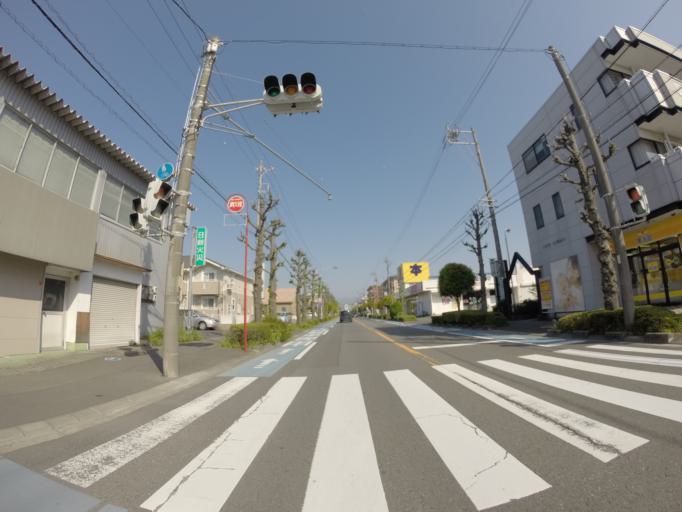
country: JP
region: Shizuoka
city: Shizuoka-shi
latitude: 34.9444
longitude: 138.3749
